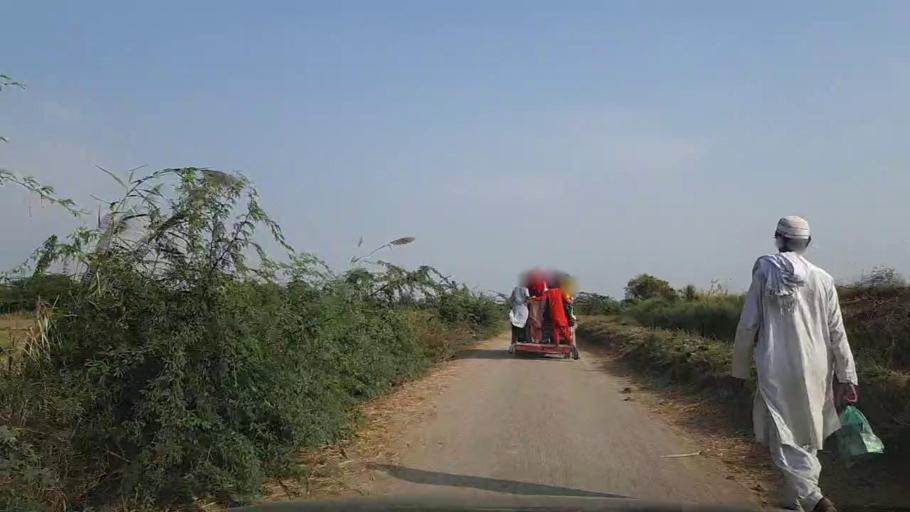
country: PK
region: Sindh
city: Thatta
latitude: 24.6477
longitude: 67.9280
